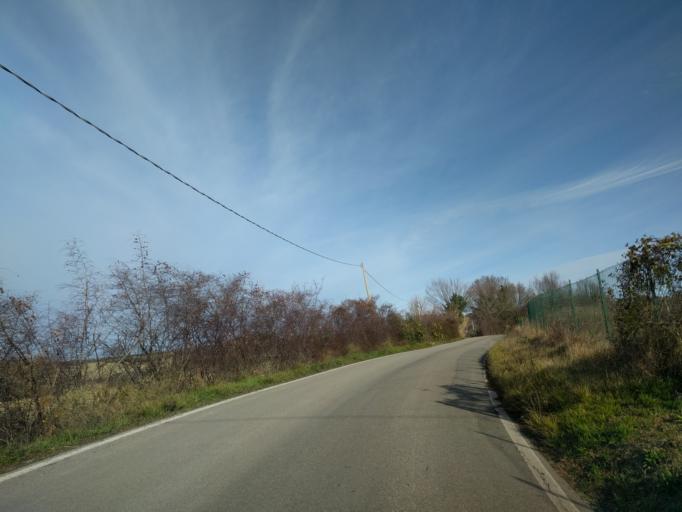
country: IT
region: The Marches
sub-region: Provincia di Pesaro e Urbino
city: Cuccurano
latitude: 43.7991
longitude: 12.9505
